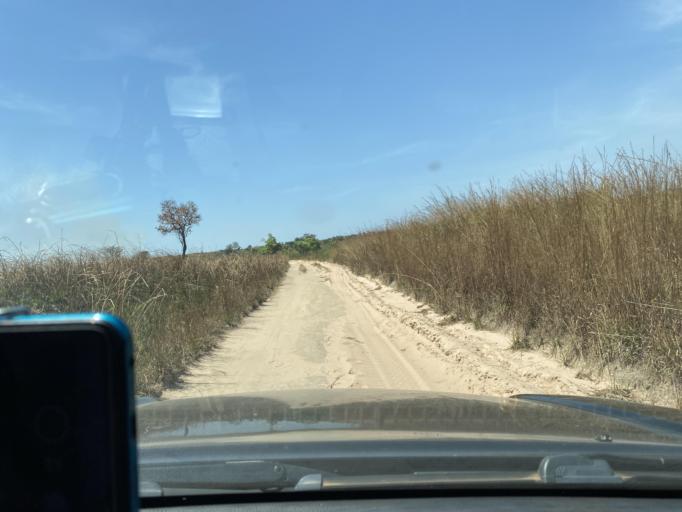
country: CD
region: Kasai-Oriental
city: Kabinda
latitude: -5.9328
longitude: 24.8293
